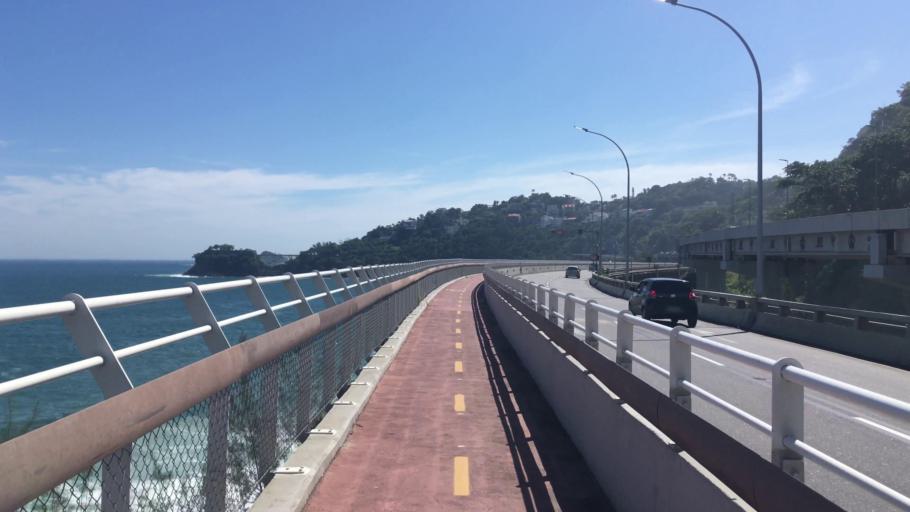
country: BR
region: Rio de Janeiro
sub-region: Rio De Janeiro
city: Rio de Janeiro
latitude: -23.0050
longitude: -43.2788
